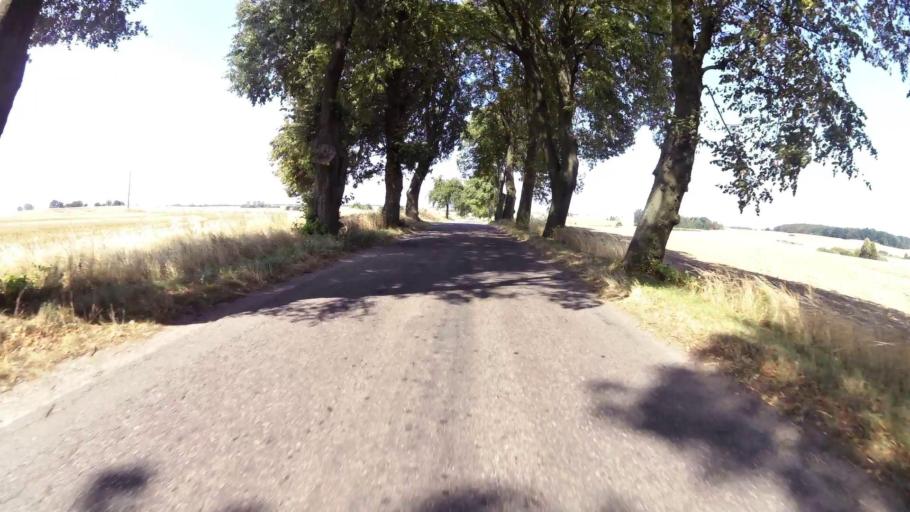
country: PL
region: West Pomeranian Voivodeship
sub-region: Powiat walecki
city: Walcz
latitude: 53.2051
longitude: 16.4860
